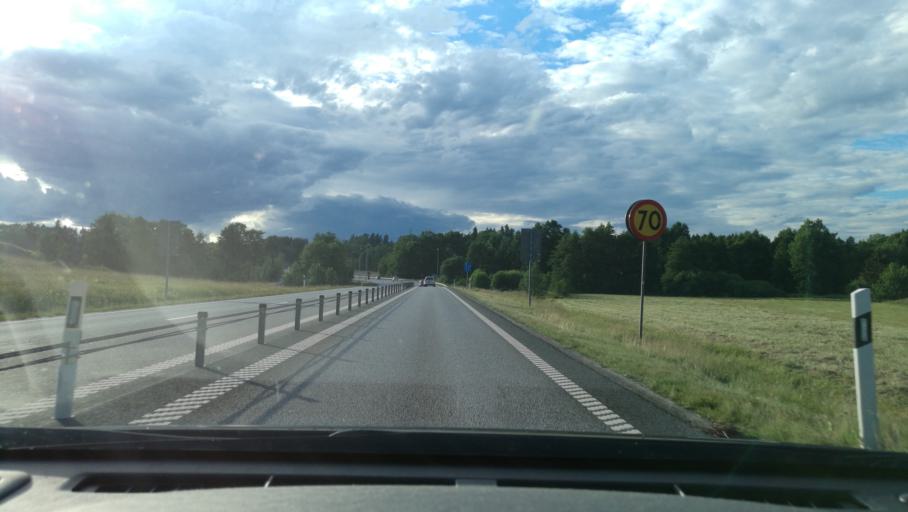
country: SE
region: OEstergoetland
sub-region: Norrkopings Kommun
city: Svartinge
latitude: 58.6890
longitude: 15.9285
